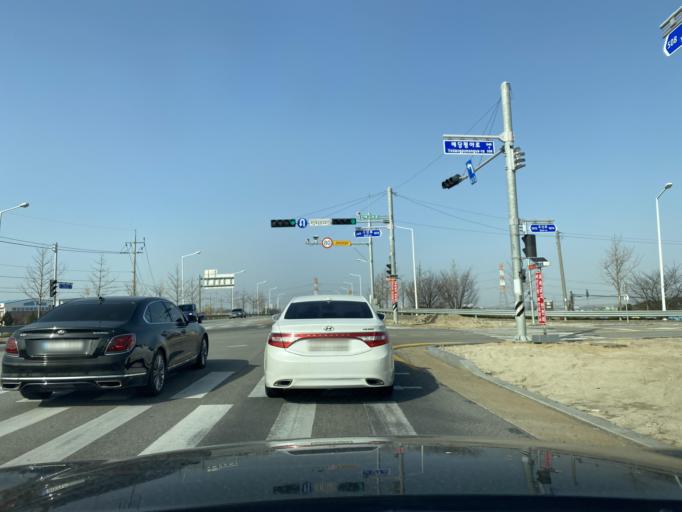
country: KR
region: Chungcheongnam-do
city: Yesan
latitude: 36.7610
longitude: 126.8130
